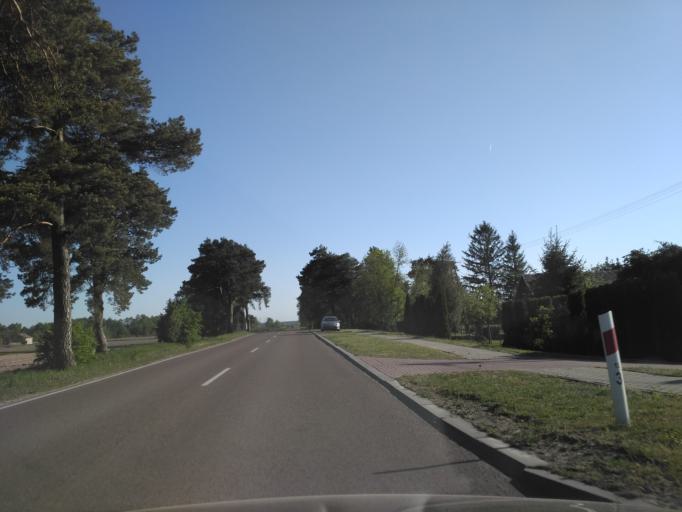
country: PL
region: Lublin Voivodeship
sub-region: Powiat swidnicki
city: Trawniki
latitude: 51.1855
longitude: 23.0535
